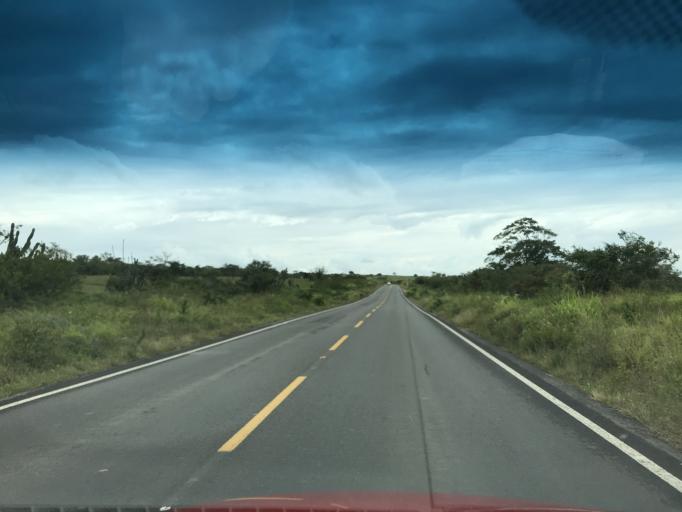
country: BR
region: Bahia
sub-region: Castro Alves
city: Castro Alves
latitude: -12.7551
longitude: -39.4112
